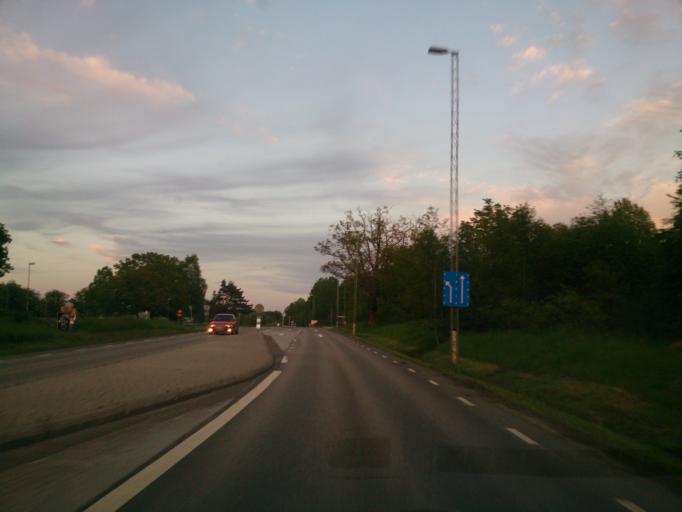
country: SE
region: OEstergoetland
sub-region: Linkopings Kommun
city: Linkoping
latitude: 58.3755
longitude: 15.6406
